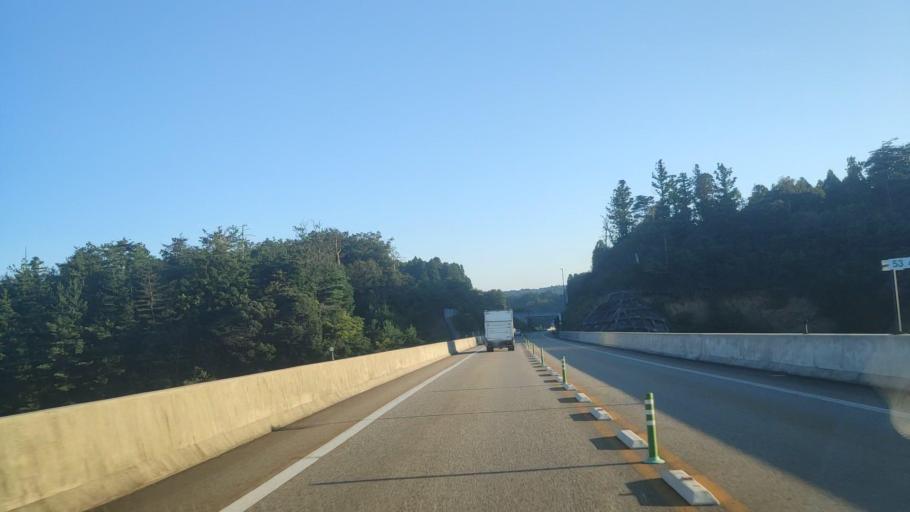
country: JP
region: Ishikawa
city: Nanao
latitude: 36.9862
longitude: 137.0473
